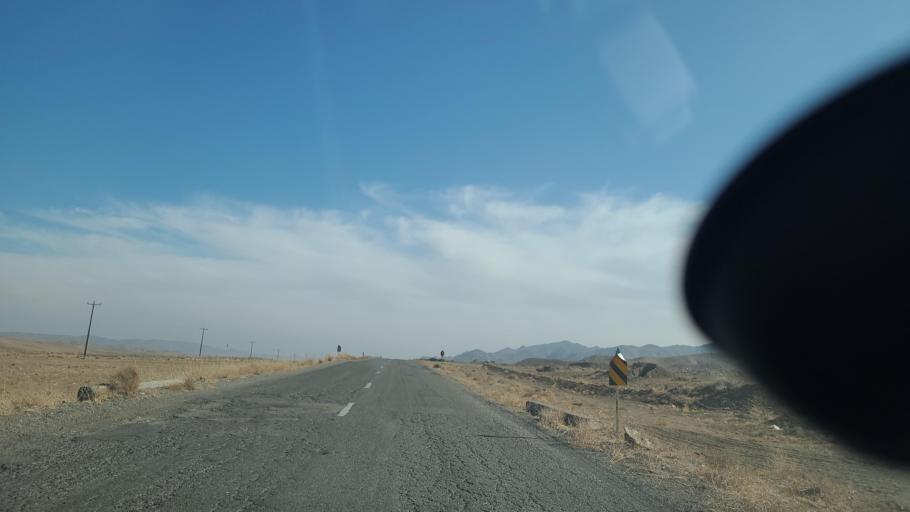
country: IR
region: Razavi Khorasan
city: Fariman
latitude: 35.5877
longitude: 59.6380
